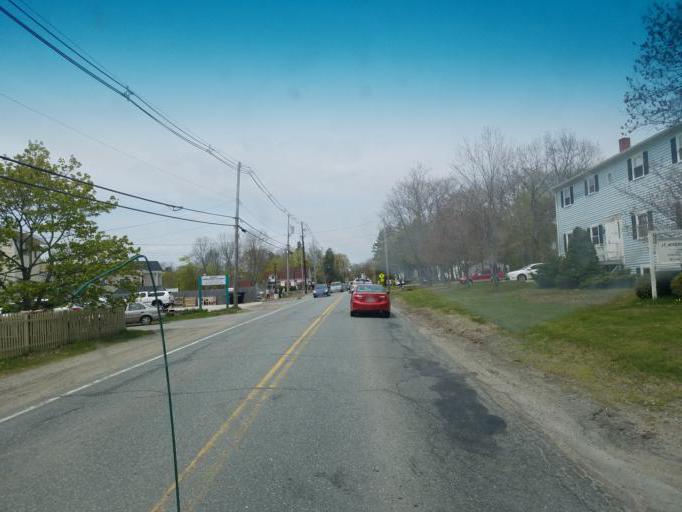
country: US
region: Maine
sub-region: Hancock County
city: Ellsworth
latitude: 44.5469
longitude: -68.4233
